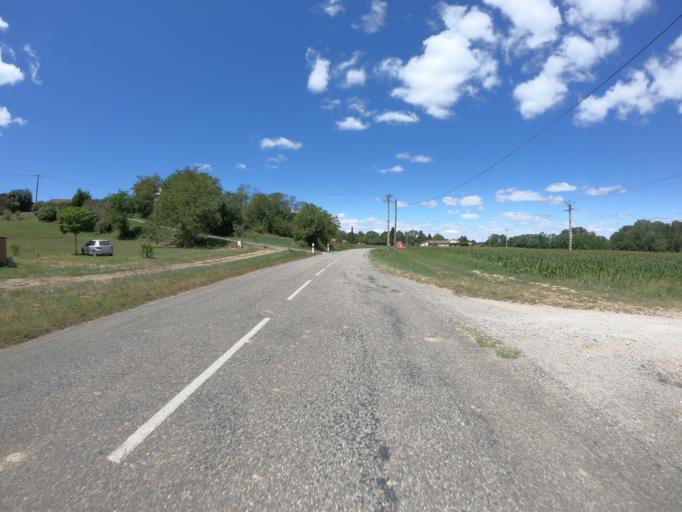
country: FR
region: Midi-Pyrenees
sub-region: Departement de l'Ariege
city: Verniolle
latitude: 43.0633
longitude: 1.7391
